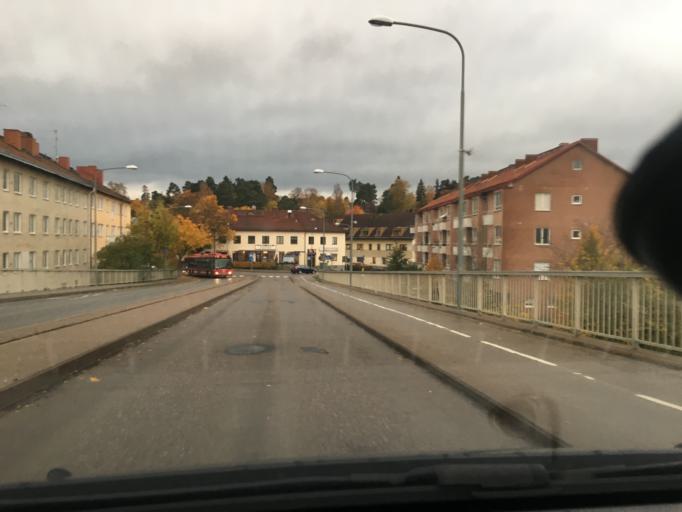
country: SE
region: Stockholm
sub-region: Stockholms Kommun
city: Kista
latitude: 59.3817
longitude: 17.9010
